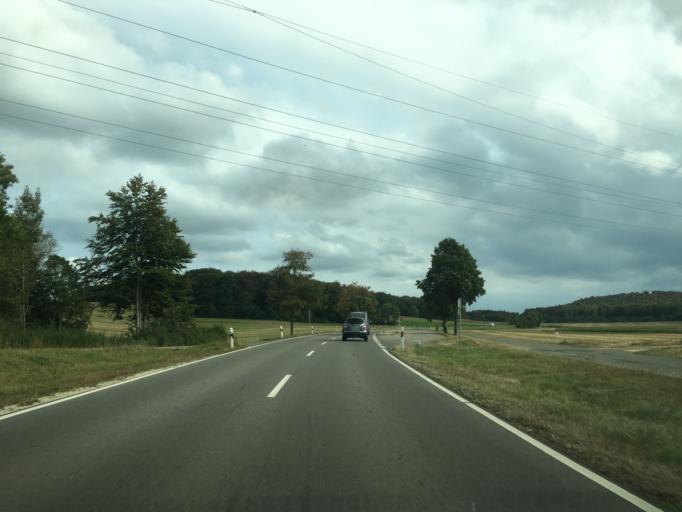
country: DE
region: Baden-Wuerttemberg
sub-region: Tuebingen Region
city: Sankt Johann
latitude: 48.3815
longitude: 9.3097
